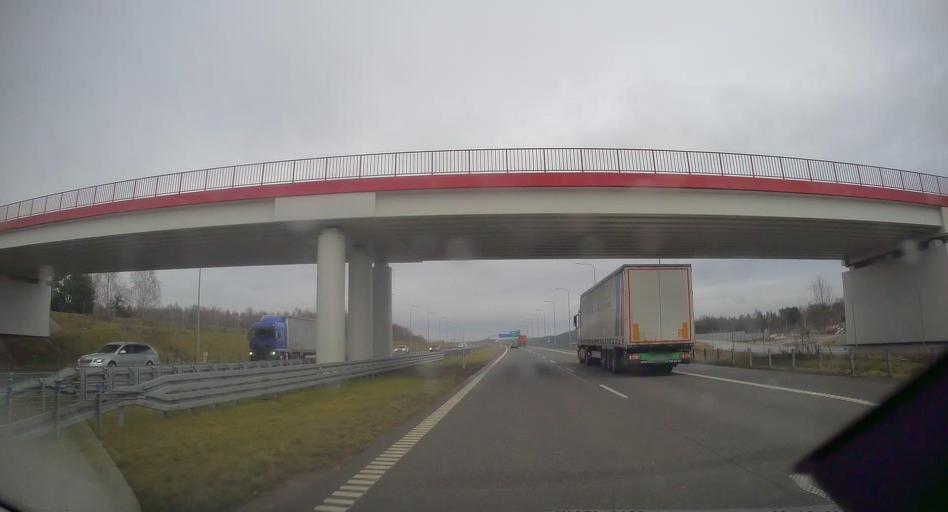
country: PL
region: Silesian Voivodeship
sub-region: Czestochowa
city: Czestochowa
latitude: 50.8751
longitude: 19.1303
